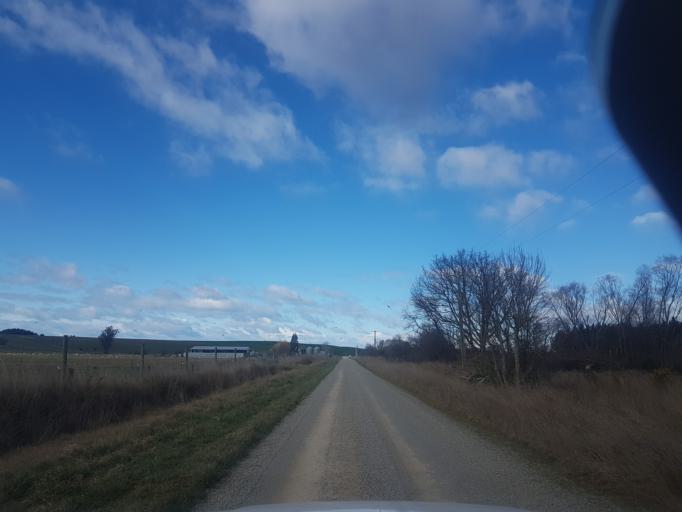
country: NZ
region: Canterbury
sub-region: Timaru District
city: Pleasant Point
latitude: -44.1904
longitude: 171.1978
